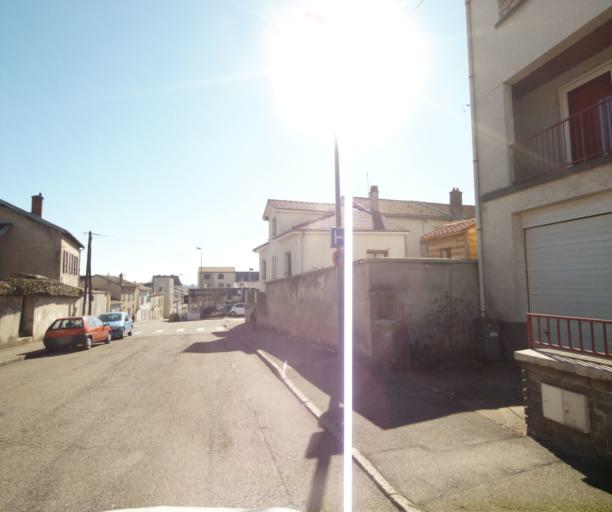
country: FR
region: Lorraine
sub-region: Departement de Meurthe-et-Moselle
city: Saint-Max
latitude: 48.7026
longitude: 6.2022
